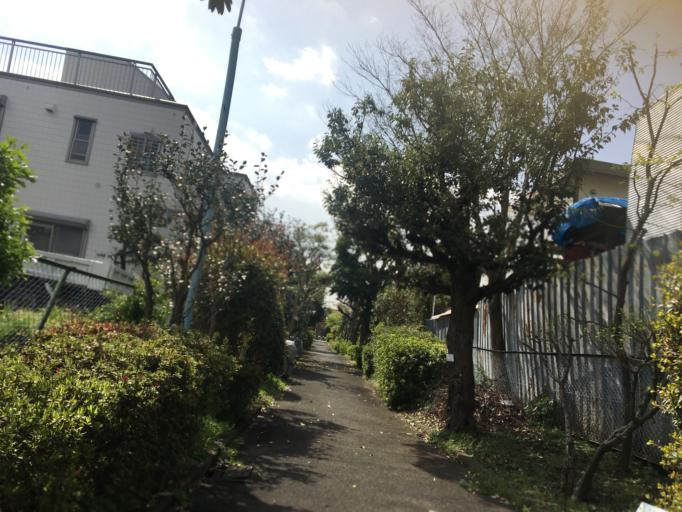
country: JP
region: Tokyo
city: Musashino
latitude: 35.7234
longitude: 139.6066
